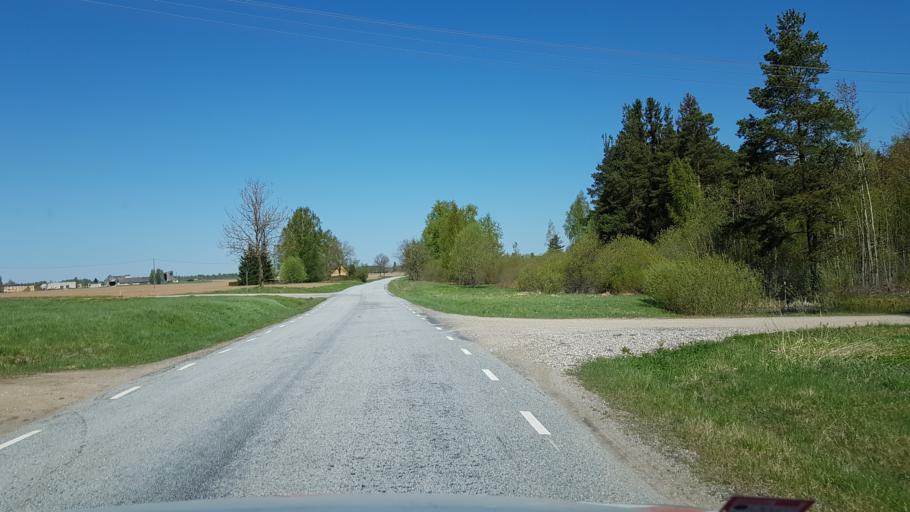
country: EE
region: Vorumaa
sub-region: Voru linn
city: Voru
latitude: 57.9118
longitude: 26.9580
